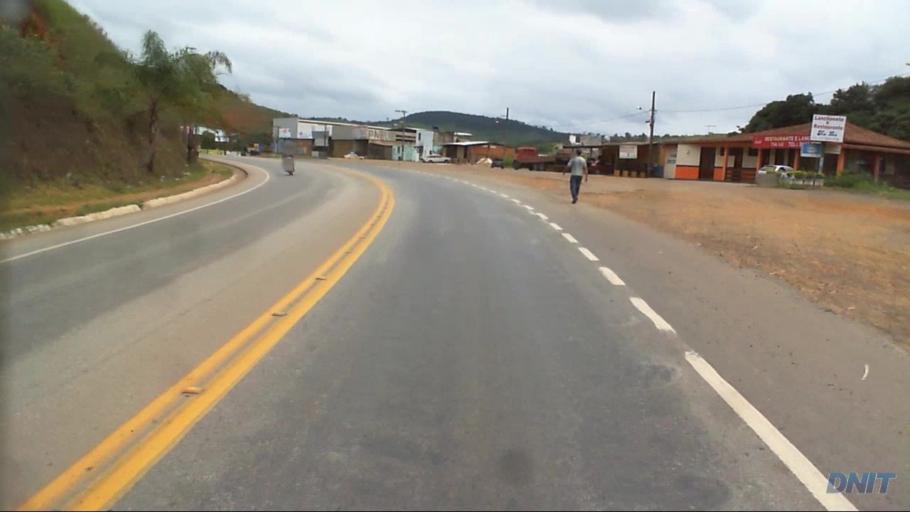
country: BR
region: Minas Gerais
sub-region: Joao Monlevade
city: Joao Monlevade
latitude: -19.8373
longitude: -43.1885
